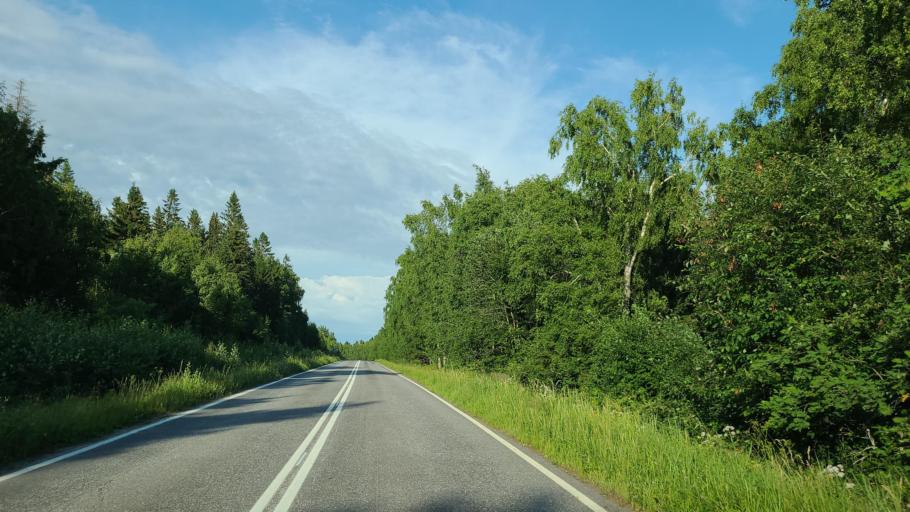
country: FI
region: Ostrobothnia
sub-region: Vaasa
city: Replot
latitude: 63.2897
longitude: 21.3432
